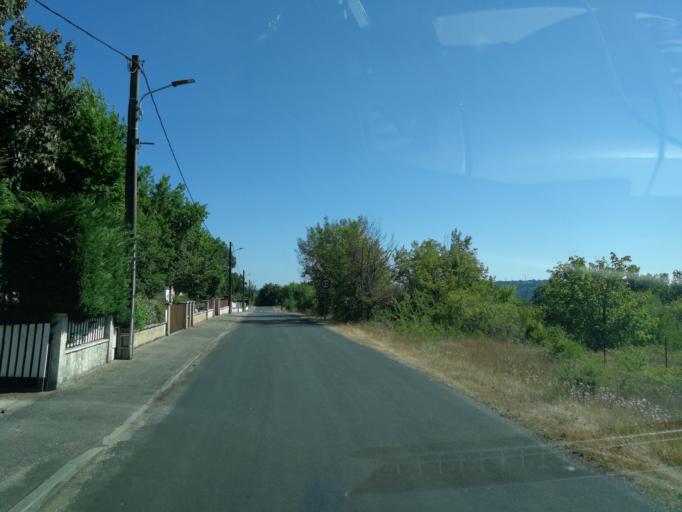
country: FR
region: Midi-Pyrenees
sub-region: Departement du Lot
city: Souillac
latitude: 44.9126
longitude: 1.4819
